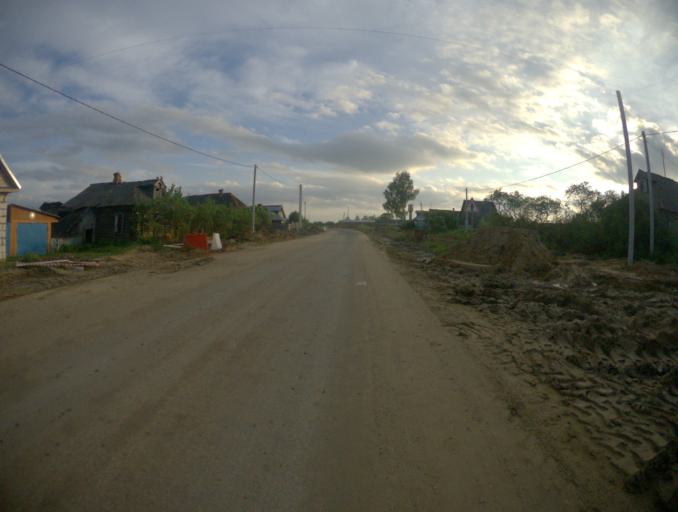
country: RU
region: Vladimir
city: Anopino
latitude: 55.6375
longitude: 40.8090
